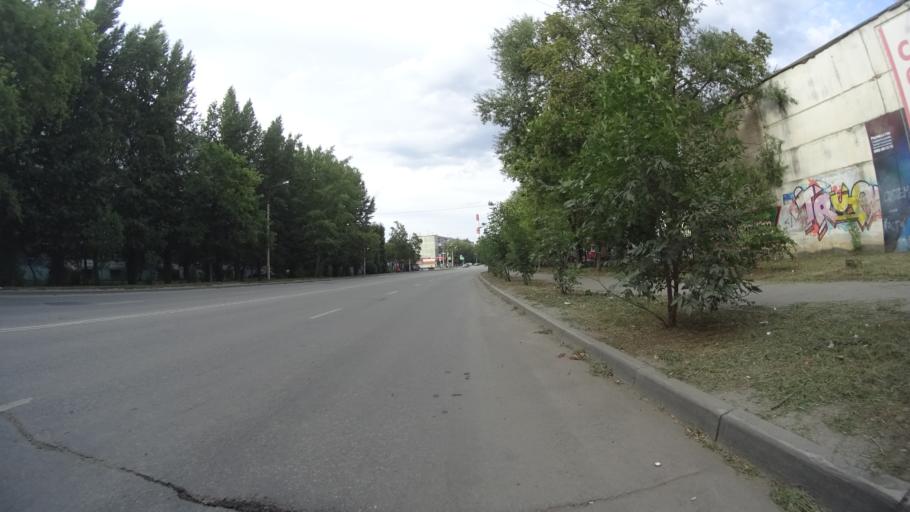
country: RU
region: Chelyabinsk
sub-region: Gorod Chelyabinsk
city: Chelyabinsk
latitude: 55.1973
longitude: 61.3180
